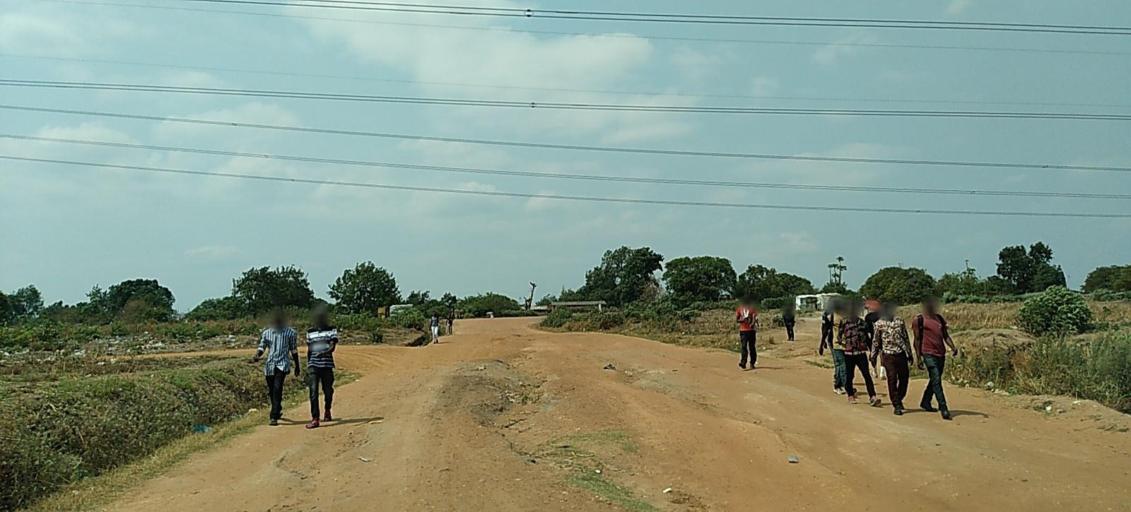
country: ZM
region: Copperbelt
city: Chambishi
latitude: -12.6341
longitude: 28.0695
